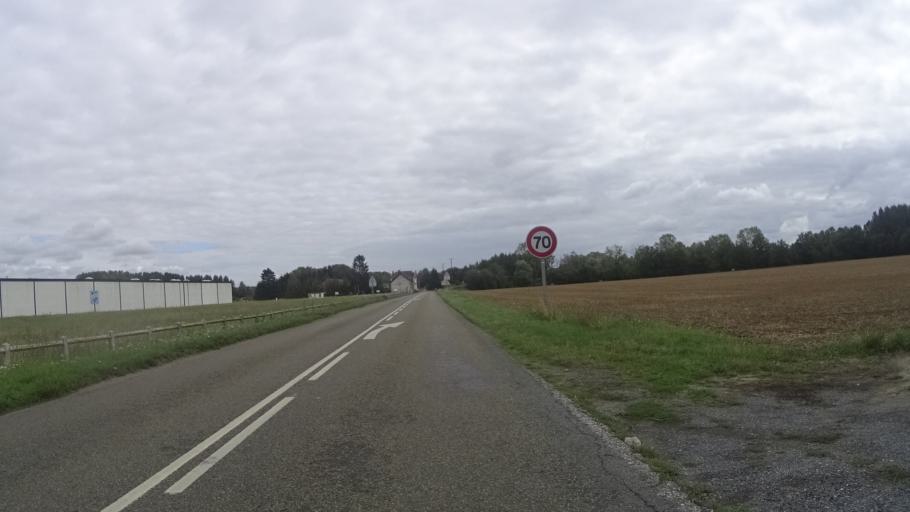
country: FR
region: Picardie
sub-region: Departement de l'Oise
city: Chiry-Ourscamp
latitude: 49.5346
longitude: 2.9562
